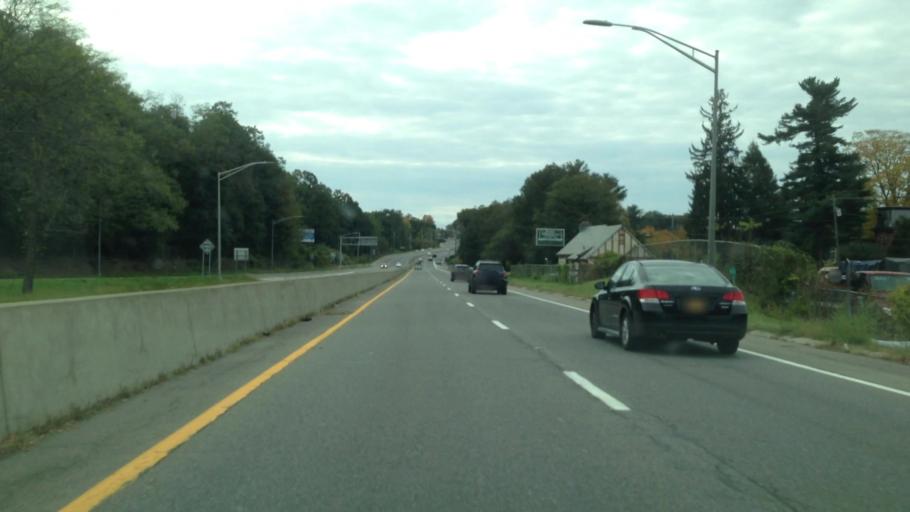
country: US
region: New York
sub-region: Dutchess County
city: Poughkeepsie
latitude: 41.6864
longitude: -73.9306
